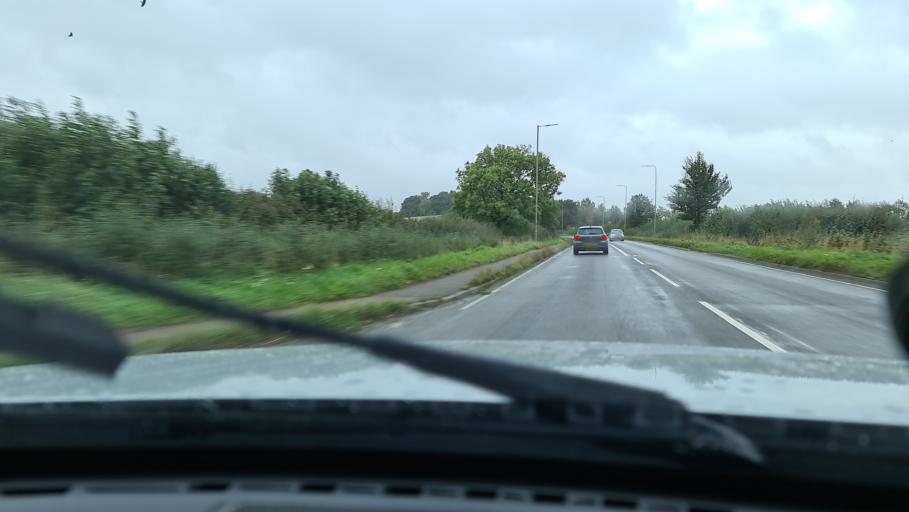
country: GB
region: England
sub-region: Oxfordshire
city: Adderbury
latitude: 52.0308
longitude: -1.3151
